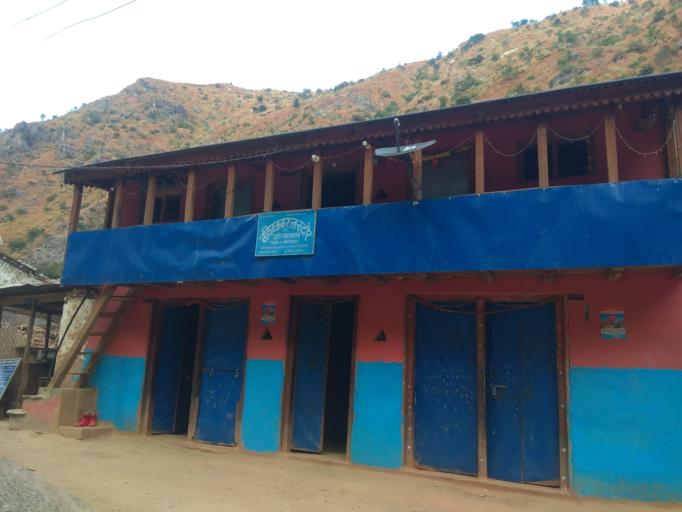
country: NP
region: Far Western
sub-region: Seti Zone
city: Achham
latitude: 29.2203
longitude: 81.6314
